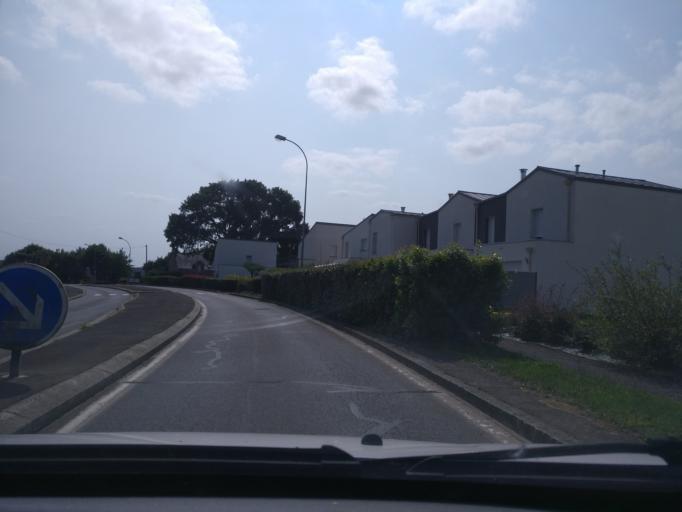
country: FR
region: Brittany
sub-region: Departement d'Ille-et-Vilaine
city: Gosne
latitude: 48.2455
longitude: -1.4607
